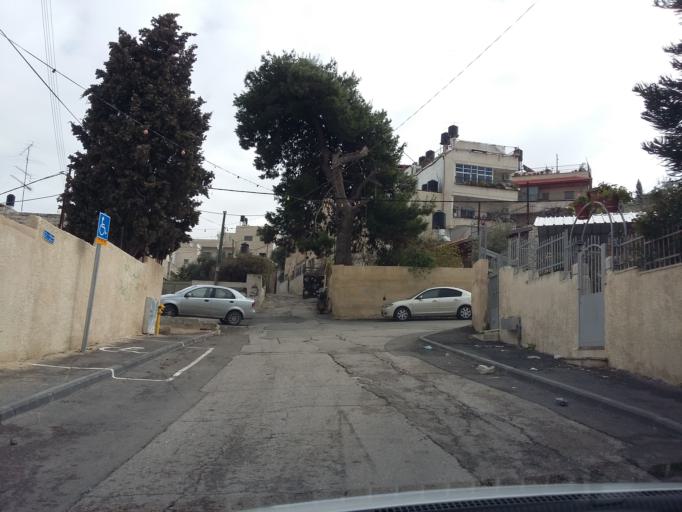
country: PS
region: West Bank
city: East Jerusalem
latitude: 31.7854
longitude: 35.2414
